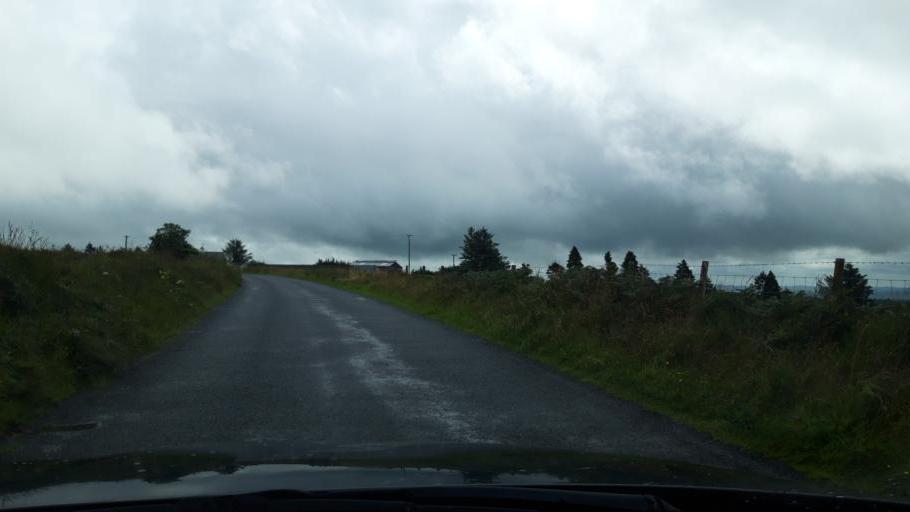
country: IE
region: Munster
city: Cahir
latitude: 52.1969
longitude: -7.9022
